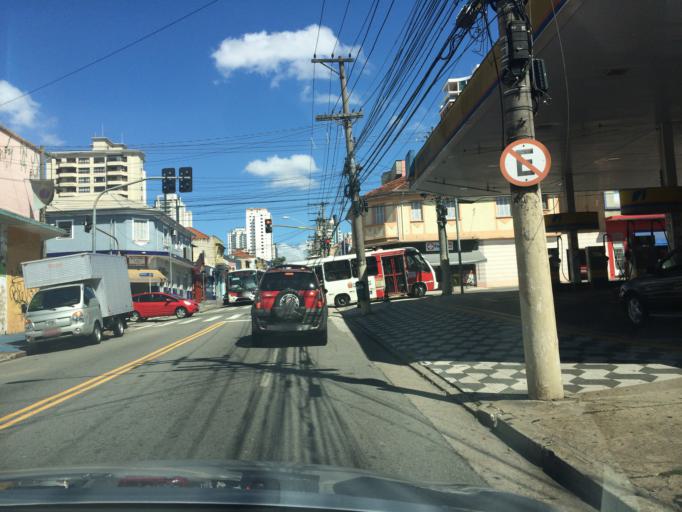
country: BR
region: Sao Paulo
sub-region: Sao Caetano Do Sul
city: Sao Caetano do Sul
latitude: -23.5464
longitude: -46.5556
